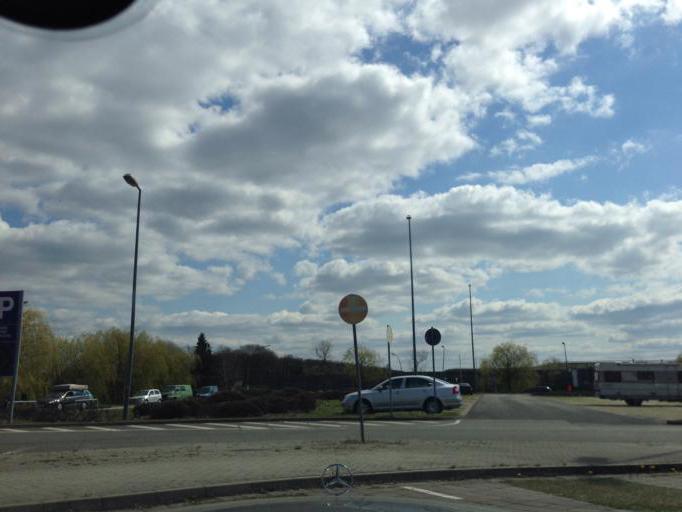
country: DE
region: Hamburg
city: Wandsbek
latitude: 53.5112
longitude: 10.0959
